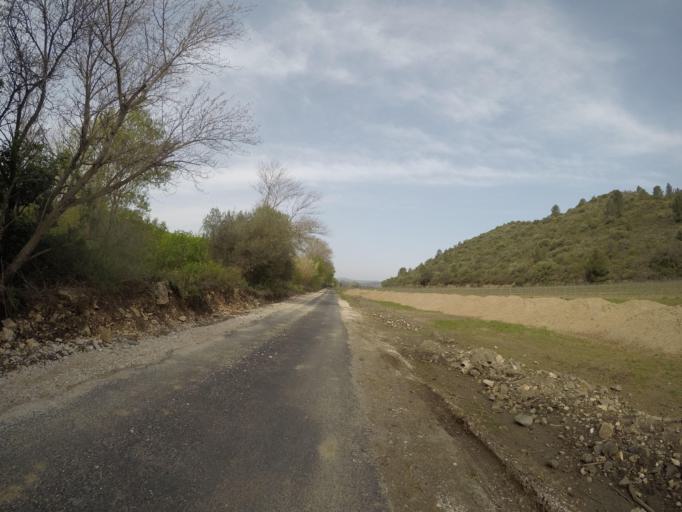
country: FR
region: Languedoc-Roussillon
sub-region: Departement des Pyrenees-Orientales
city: Estagel
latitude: 42.7748
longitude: 2.7545
